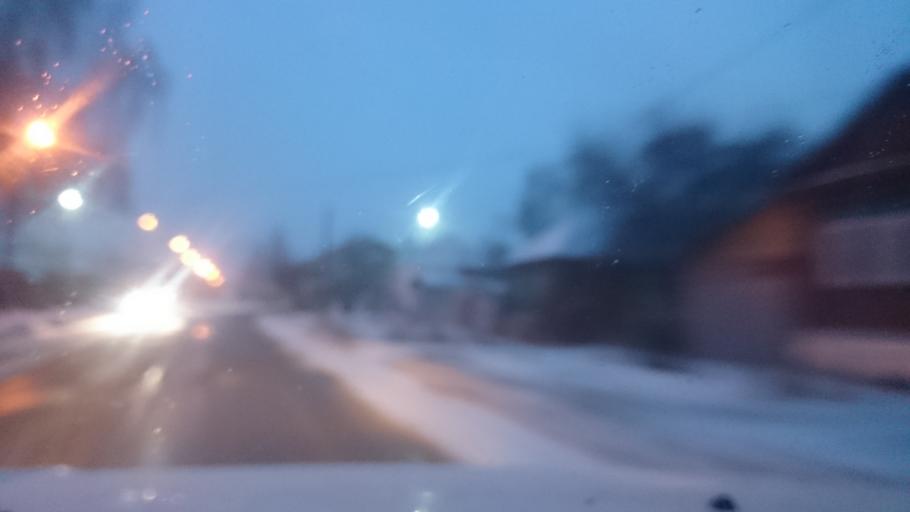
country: RU
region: Tula
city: Tula
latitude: 54.2014
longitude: 37.5383
